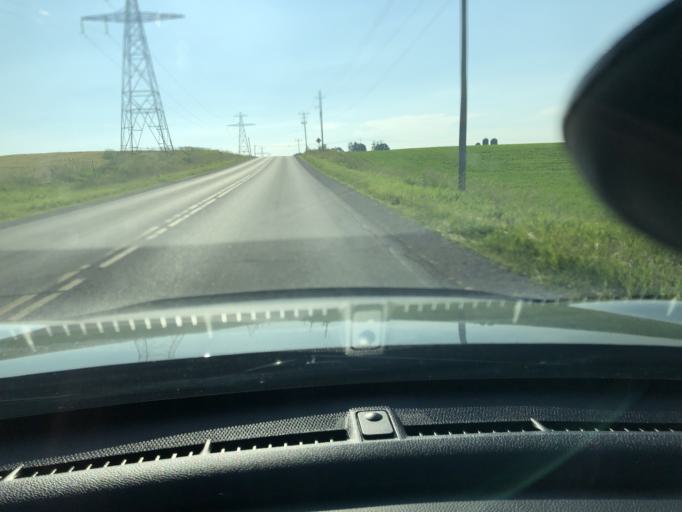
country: CA
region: Ontario
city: Stratford
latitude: 43.3885
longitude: -80.9156
